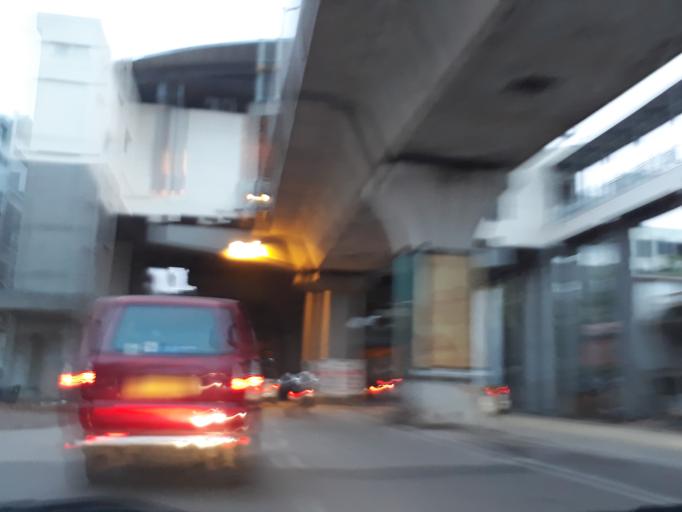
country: IN
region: Telangana
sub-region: Rangareddi
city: Kukatpalli
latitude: 17.4274
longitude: 78.4145
